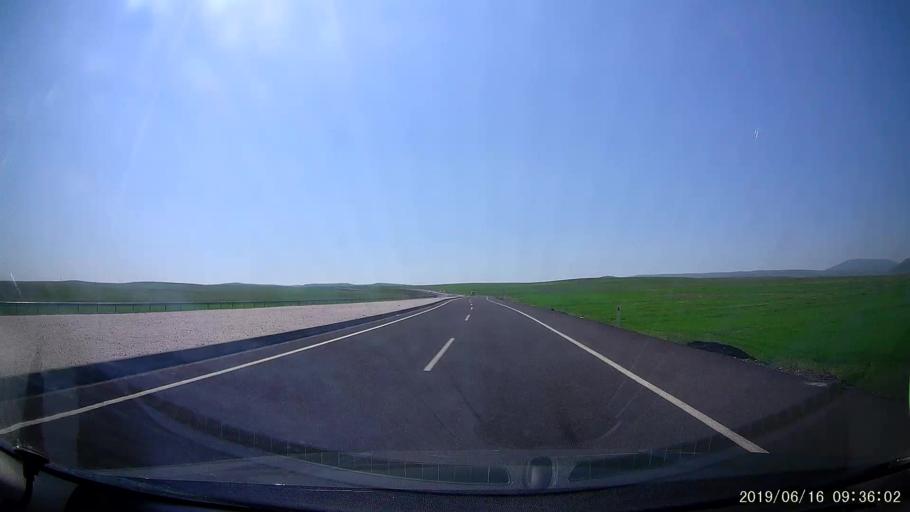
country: TR
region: Kars
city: Kars
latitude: 40.5628
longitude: 43.1654
